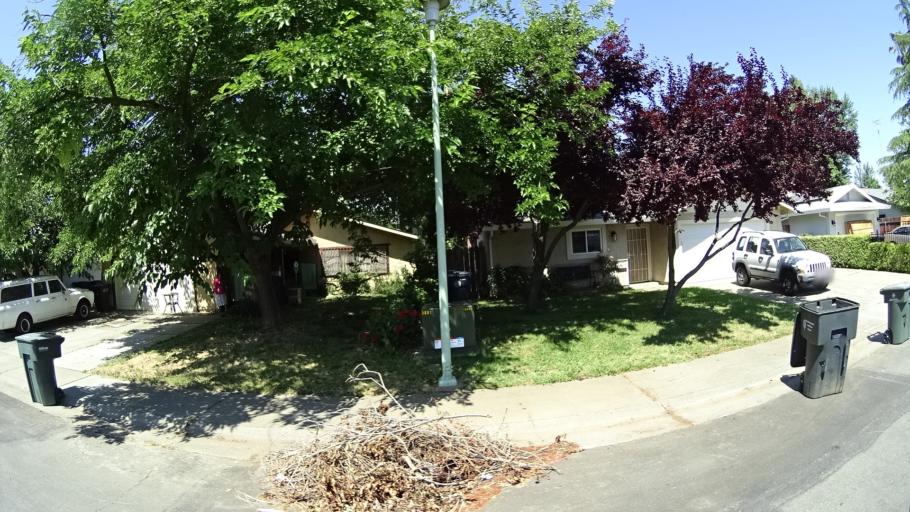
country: US
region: California
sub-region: Sacramento County
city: Florin
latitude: 38.5334
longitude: -121.4134
